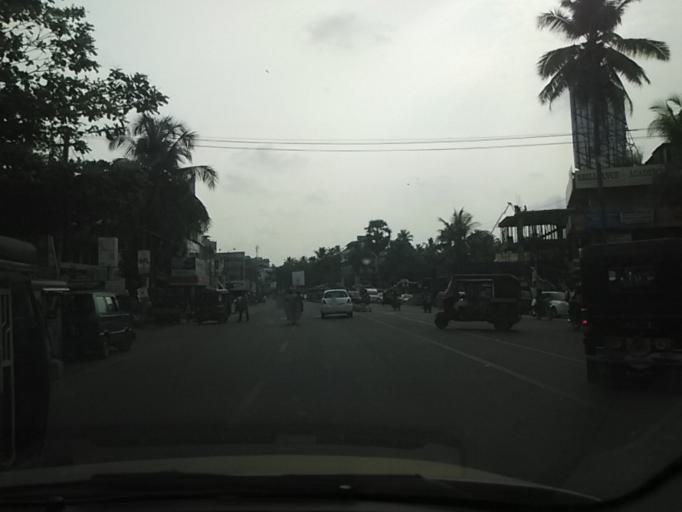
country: IN
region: Kerala
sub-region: Kozhikode
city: Kozhikode
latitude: 11.2796
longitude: 75.7852
